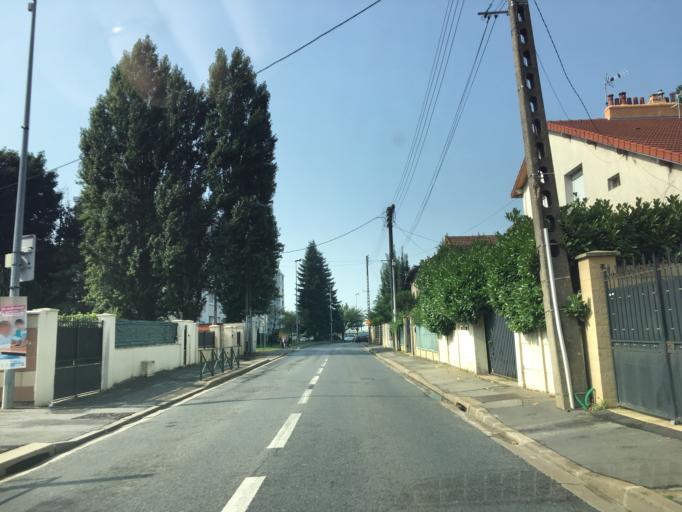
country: FR
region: Ile-de-France
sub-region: Departement du Val-de-Marne
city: Boissy-Saint-Leger
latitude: 48.7511
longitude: 2.5177
